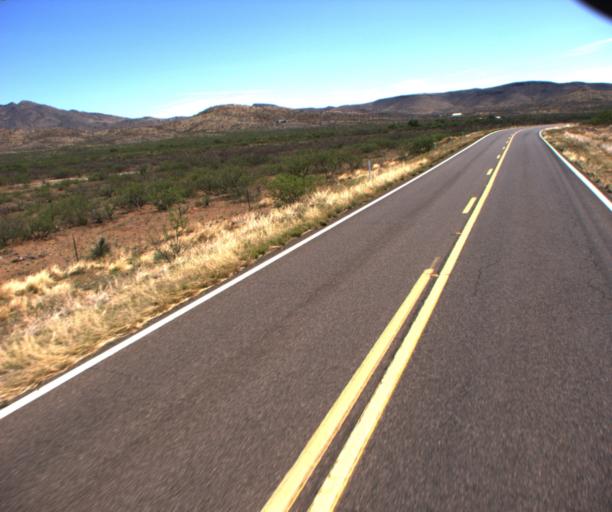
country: US
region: Arizona
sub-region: Cochise County
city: Douglas
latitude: 31.4906
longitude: -109.4297
